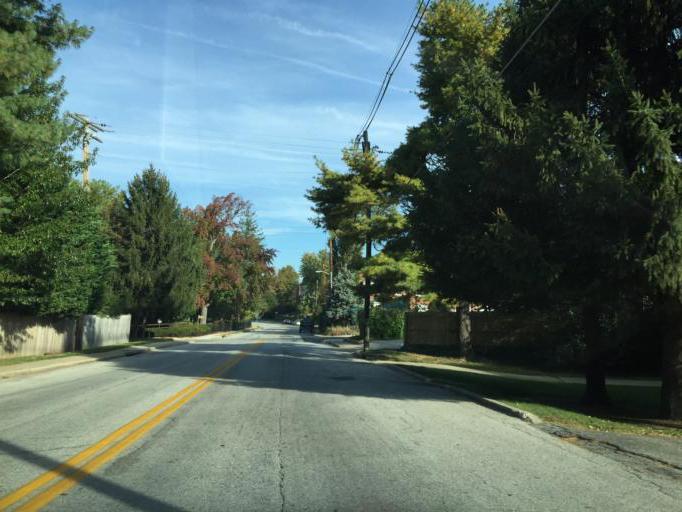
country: US
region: Maryland
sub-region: Baltimore County
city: Towson
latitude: 39.3741
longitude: -76.6189
